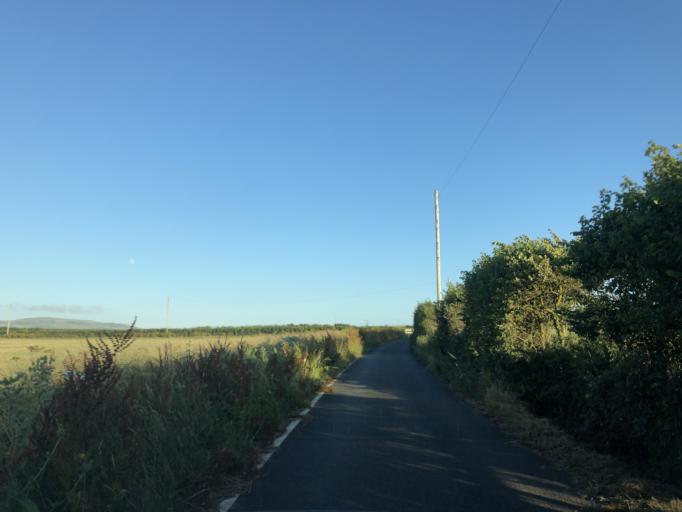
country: GB
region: England
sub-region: Isle of Wight
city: Chale
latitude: 50.6310
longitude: -1.3772
